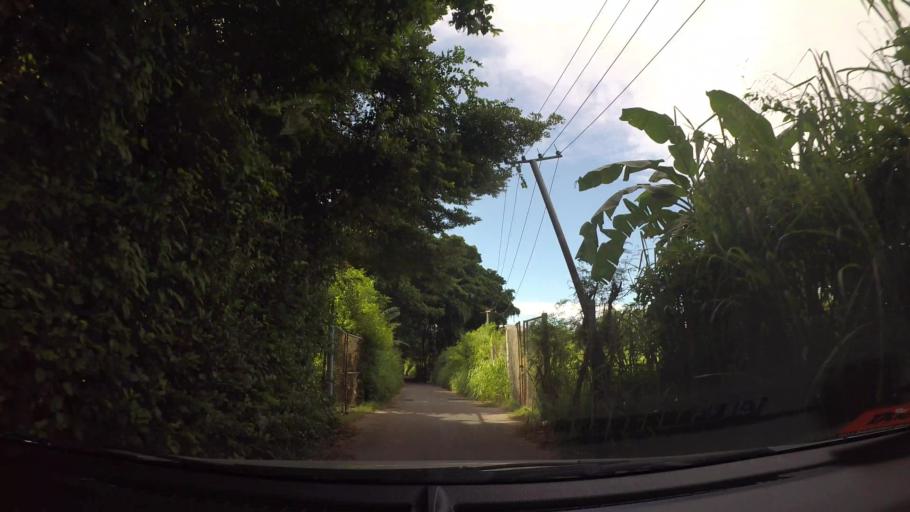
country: TH
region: Chon Buri
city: Phatthaya
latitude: 12.9175
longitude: 100.8736
